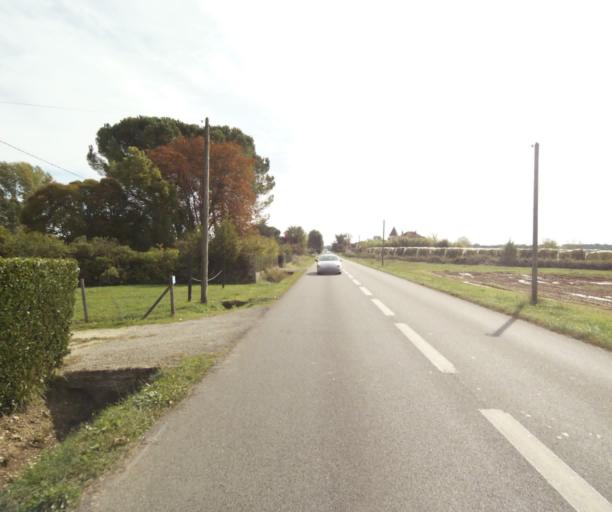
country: FR
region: Midi-Pyrenees
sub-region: Departement du Tarn-et-Garonne
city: Labastide-Saint-Pierre
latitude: 43.9256
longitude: 1.3887
